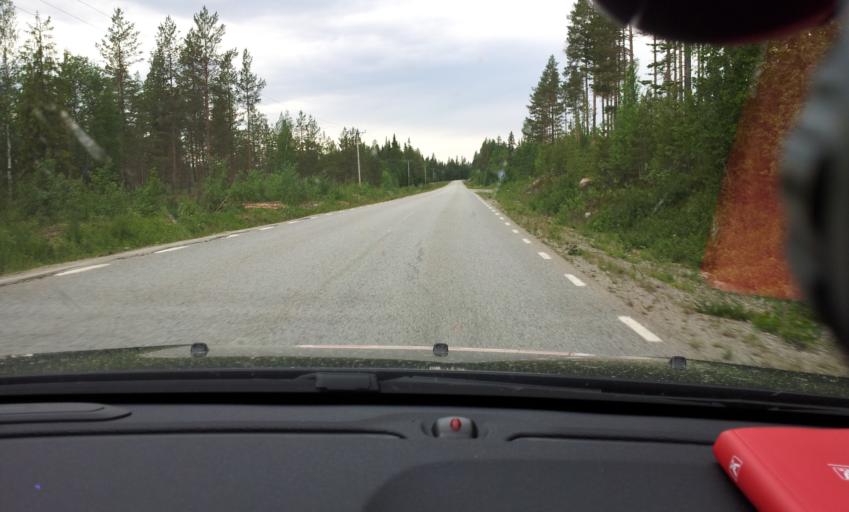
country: SE
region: Jaemtland
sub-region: Bergs Kommun
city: Hoverberg
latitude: 62.6753
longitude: 14.6869
